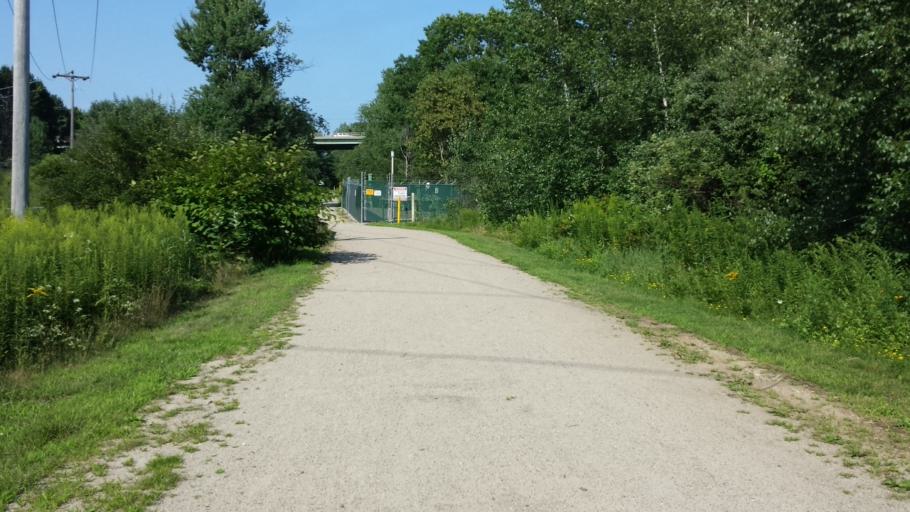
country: US
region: Maine
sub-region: York County
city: Biddeford
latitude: 43.4715
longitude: -70.4926
